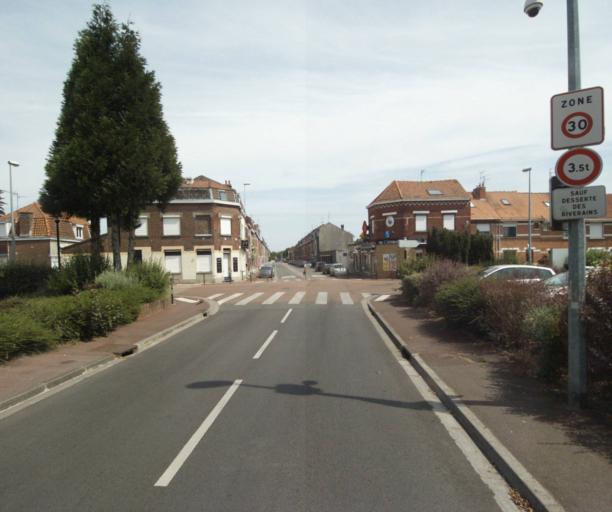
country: FR
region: Nord-Pas-de-Calais
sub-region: Departement du Nord
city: Roncq
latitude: 50.7268
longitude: 3.1276
